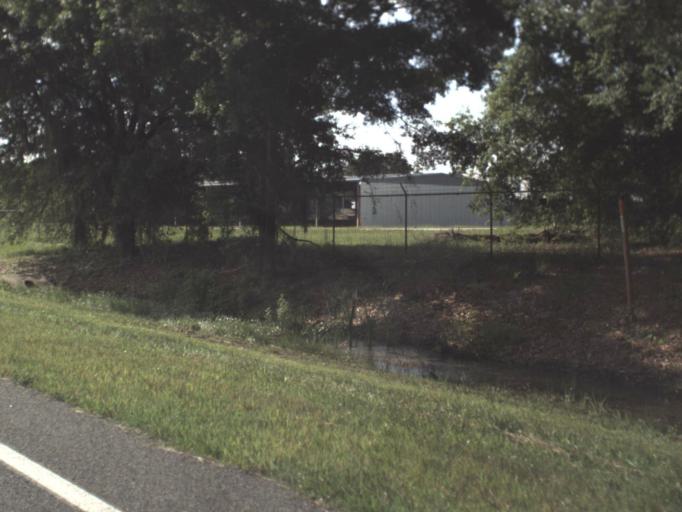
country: US
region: Florida
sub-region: Alachua County
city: Gainesville
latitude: 29.5103
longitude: -82.2753
